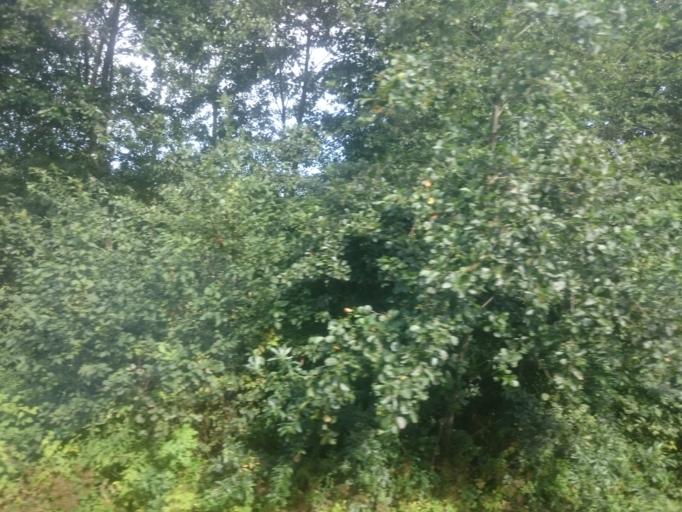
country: RU
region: Kaliningrad
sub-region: Zelenogradskiy Rayon
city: Zelenogradsk
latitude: 54.9437
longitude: 20.4133
